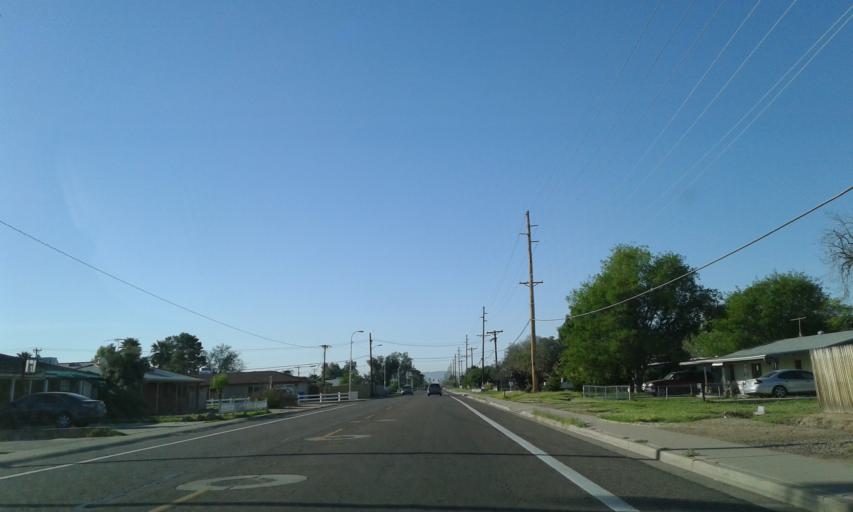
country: US
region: Arizona
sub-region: Maricopa County
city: Glendale
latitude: 33.5217
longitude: -112.1083
